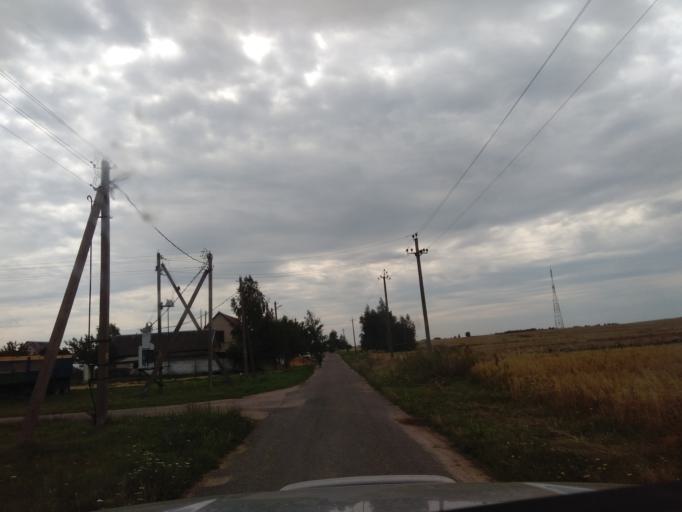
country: BY
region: Minsk
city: Kapyl'
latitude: 53.1568
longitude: 27.0658
